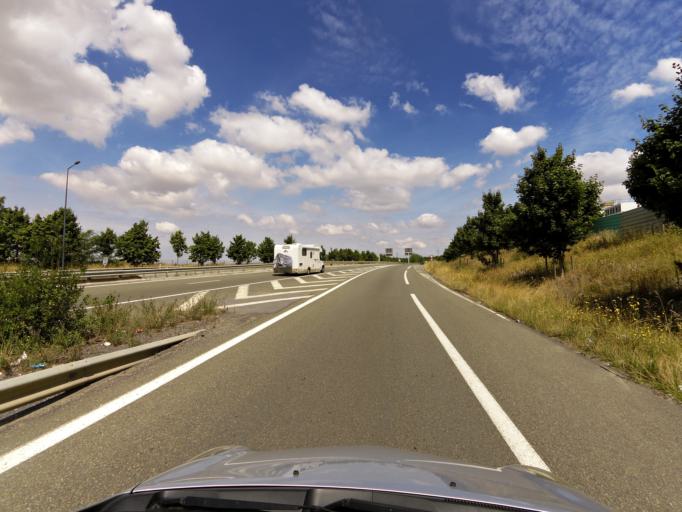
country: FR
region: Ile-de-France
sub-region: Departement de Seine-et-Marne
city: Chauconin-Neufmontiers
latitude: 48.9581
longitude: 2.8587
